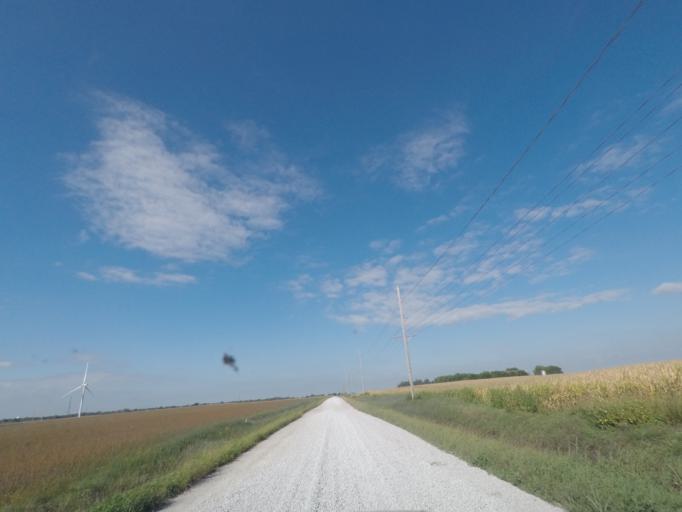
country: US
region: Iowa
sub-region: Story County
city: Nevada
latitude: 42.0345
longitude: -93.4177
